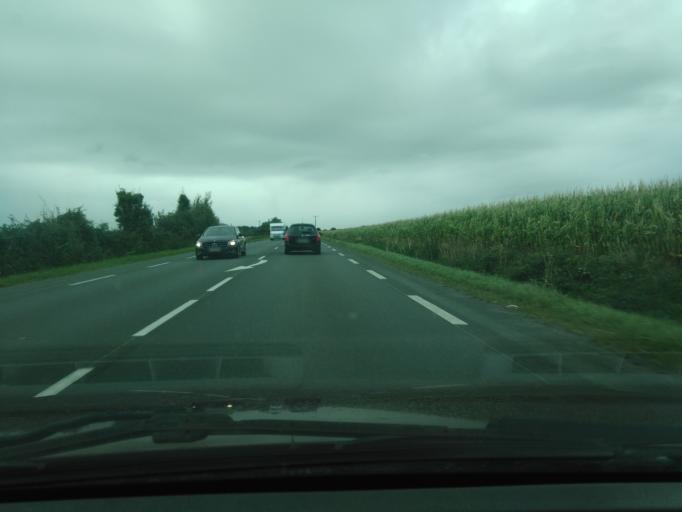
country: FR
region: Pays de la Loire
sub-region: Departement de la Vendee
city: Sainte-Gemme-la-Plaine
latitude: 46.4554
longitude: -1.1051
